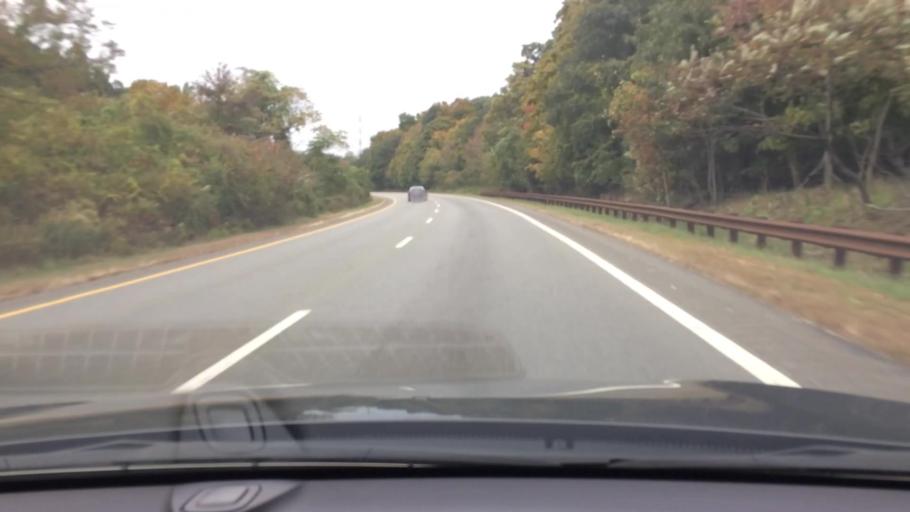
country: US
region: New Jersey
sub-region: Bergen County
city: Alpine
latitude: 40.9435
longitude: -73.9220
